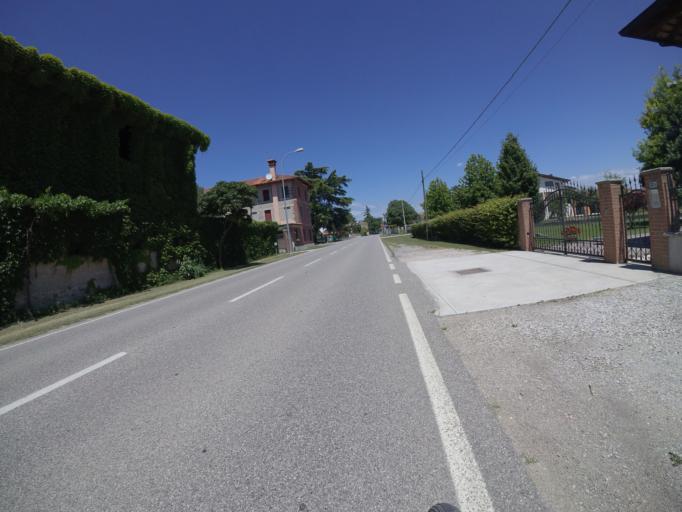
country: IT
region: Friuli Venezia Giulia
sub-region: Provincia di Udine
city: Talmassons
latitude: 45.9319
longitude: 13.0907
